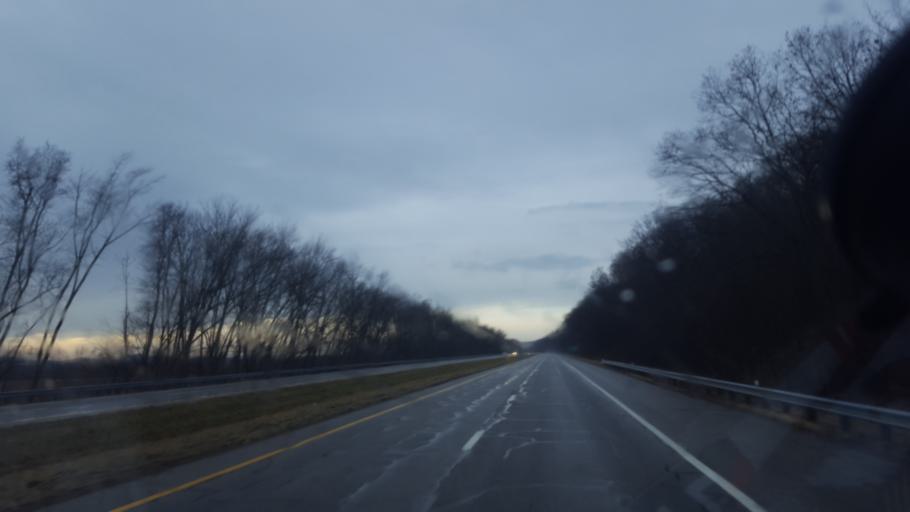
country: US
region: Ohio
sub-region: Tuscarawas County
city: Newcomerstown
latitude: 40.2823
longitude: -81.6578
